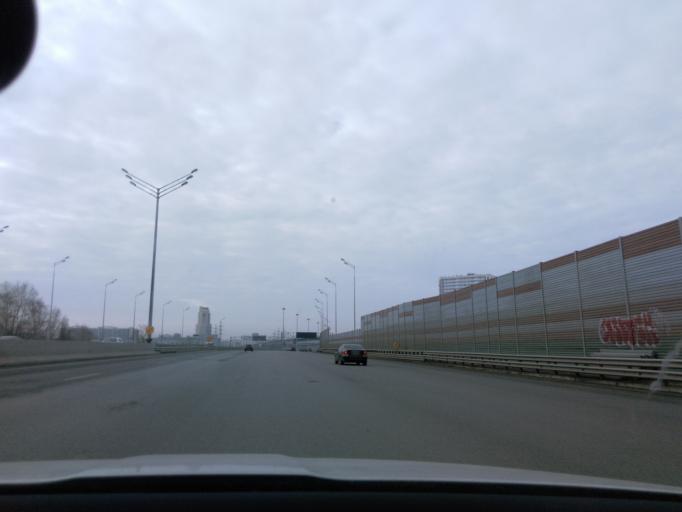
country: RU
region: Moskovskaya
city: Levoberezhnaya
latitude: 55.8935
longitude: 37.4855
